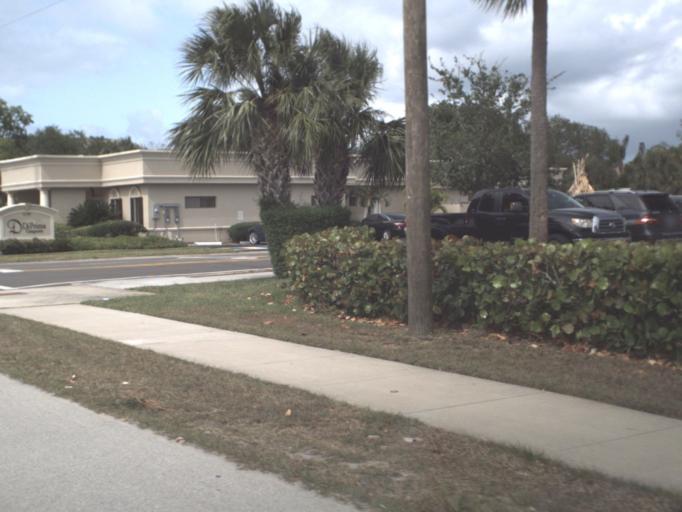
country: US
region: Florida
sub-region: Brevard County
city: Satellite Beach
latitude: 28.1793
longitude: -80.6060
